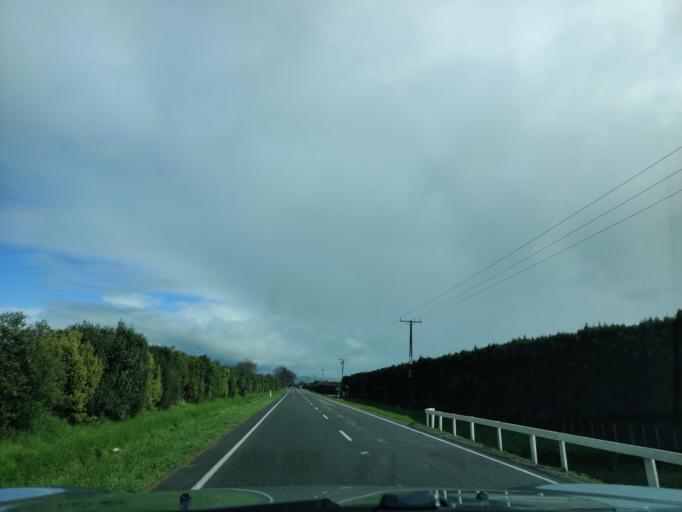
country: NZ
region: Hawke's Bay
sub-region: Hastings District
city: Hastings
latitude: -39.6814
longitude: 176.8191
